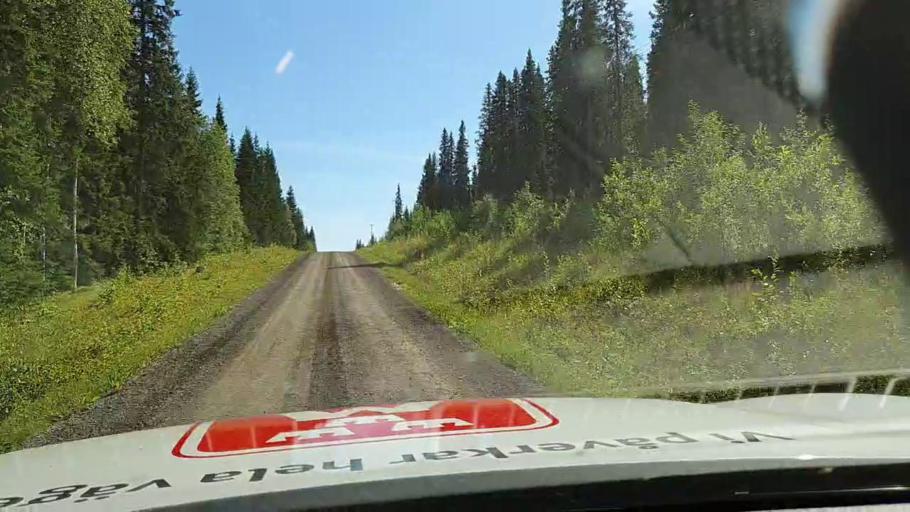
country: SE
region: Jaemtland
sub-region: Stroemsunds Kommun
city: Stroemsund
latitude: 63.7806
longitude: 15.3108
